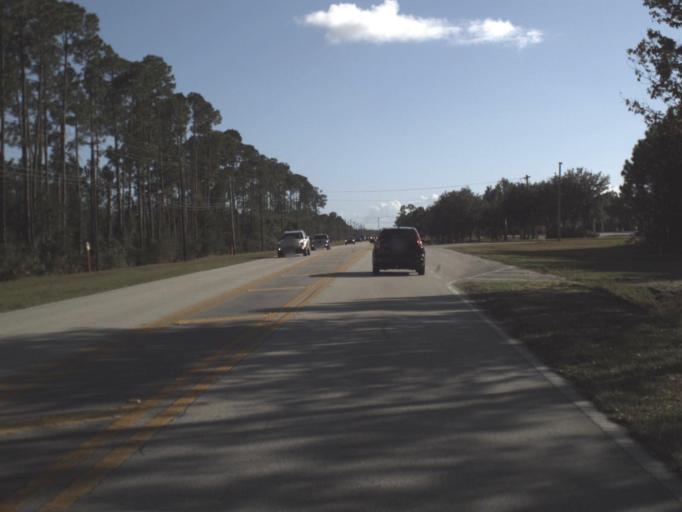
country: US
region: Florida
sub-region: Volusia County
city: Holly Hill
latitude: 29.2344
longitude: -81.0974
